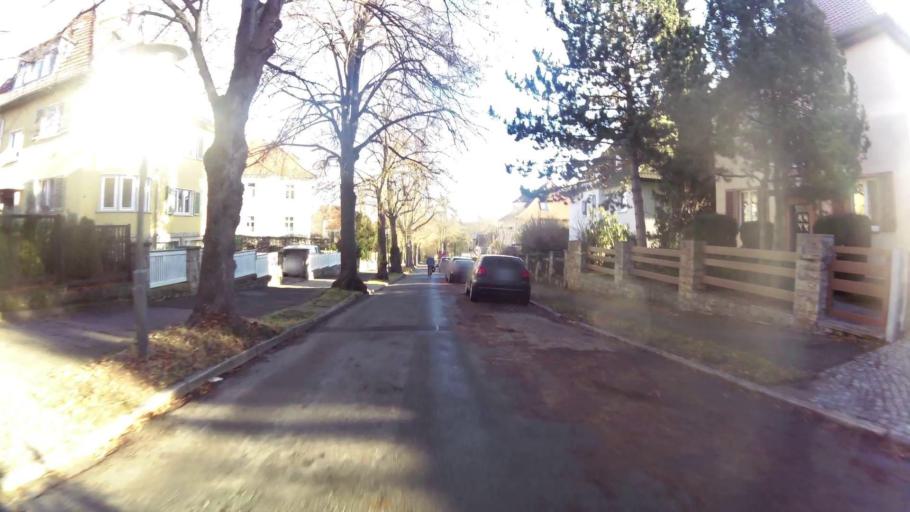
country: DE
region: Thuringia
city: Weimar
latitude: 50.9637
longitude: 11.3330
